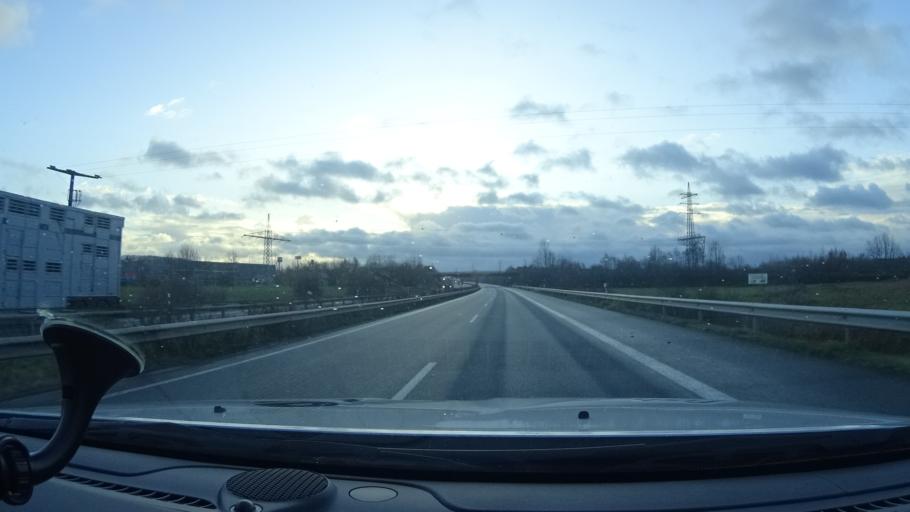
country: DE
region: North Rhine-Westphalia
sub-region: Regierungsbezirk Munster
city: Rheine
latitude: 52.3313
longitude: 7.4168
